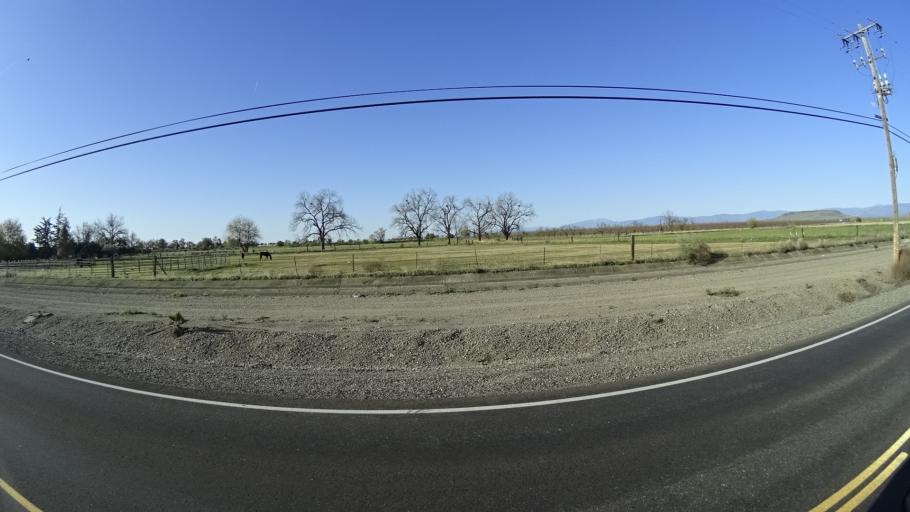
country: US
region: California
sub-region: Glenn County
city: Orland
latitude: 39.7674
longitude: -122.2492
